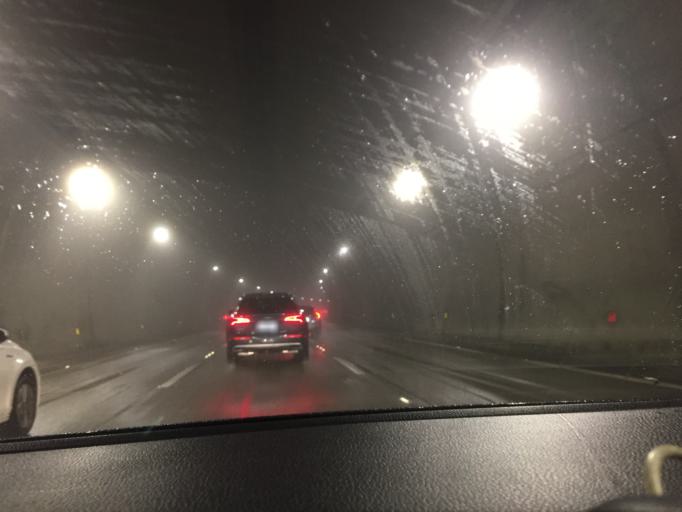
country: BR
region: Sao Paulo
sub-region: Cubatao
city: Cubatao
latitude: -23.9174
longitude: -46.5298
